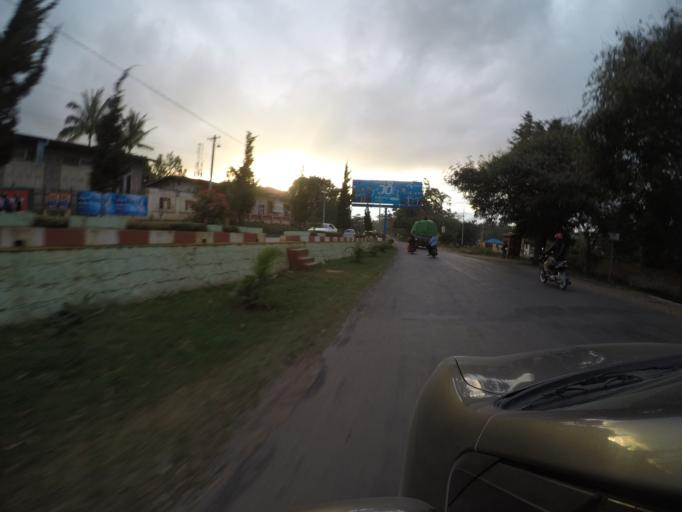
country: MM
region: Shan
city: Taunggyi
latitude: 20.7925
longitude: 97.0134
